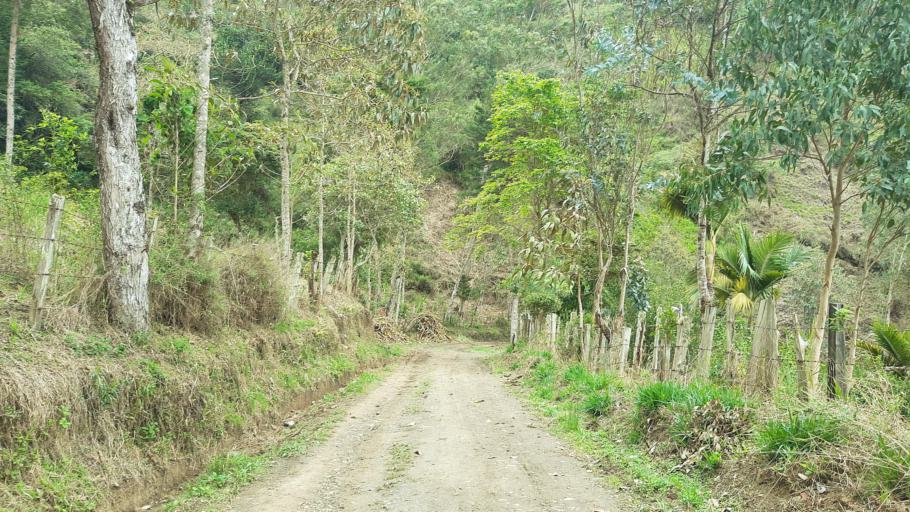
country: CO
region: Boyaca
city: Garagoa
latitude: 5.0544
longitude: -73.3497
